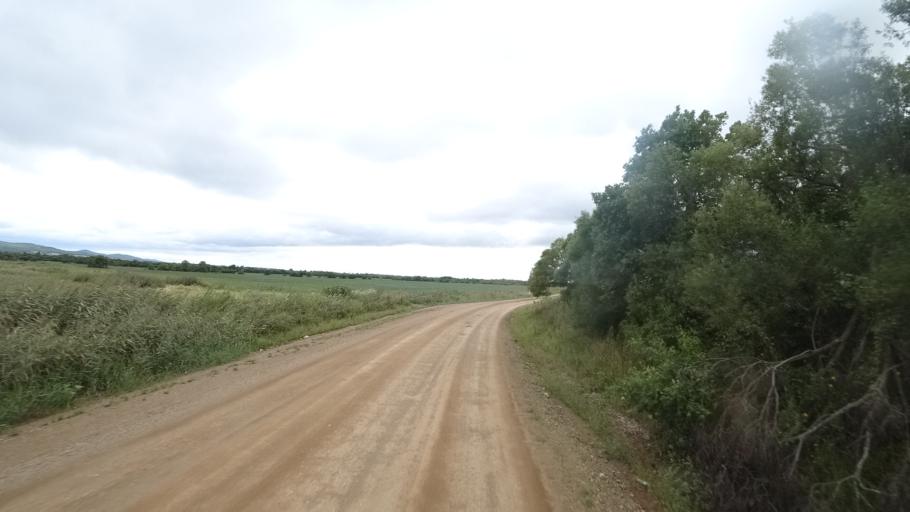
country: RU
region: Primorskiy
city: Chernigovka
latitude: 44.3434
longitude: 132.6126
